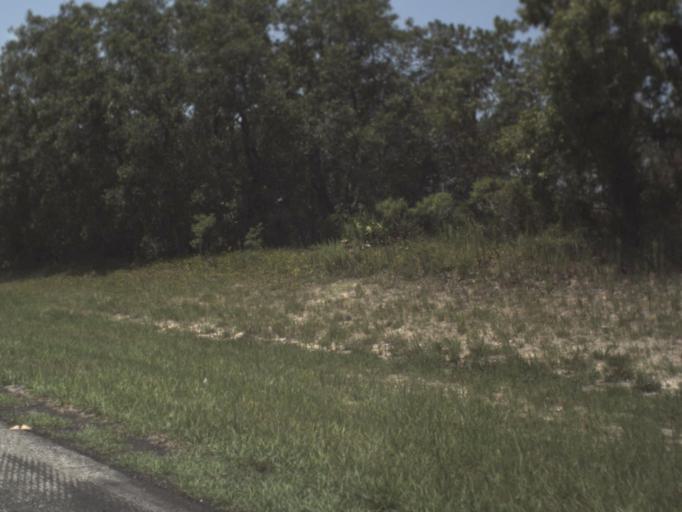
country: US
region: Florida
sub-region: Hernando County
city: North Weeki Wachee
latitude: 28.6361
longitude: -82.5522
